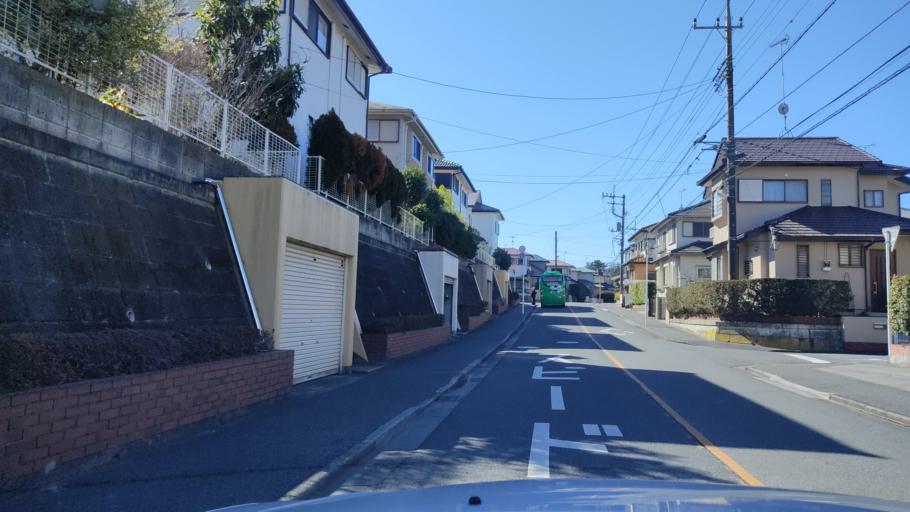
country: JP
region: Chiba
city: Nagareyama
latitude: 35.9068
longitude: 139.9165
